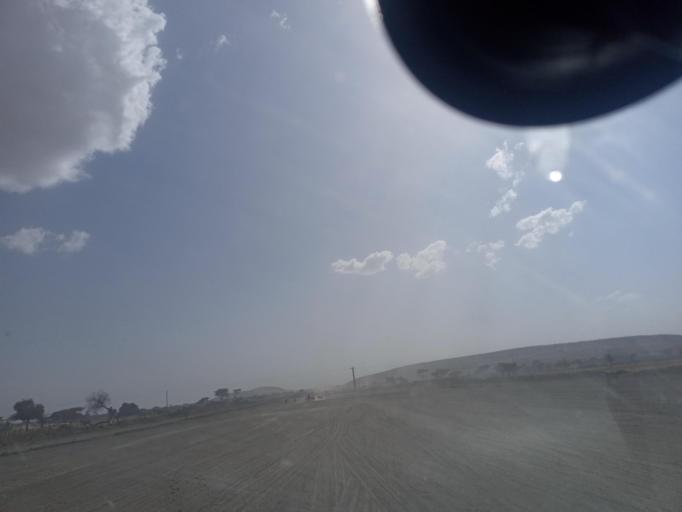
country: ET
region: Oromiya
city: Ziway
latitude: 7.8291
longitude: 38.6501
